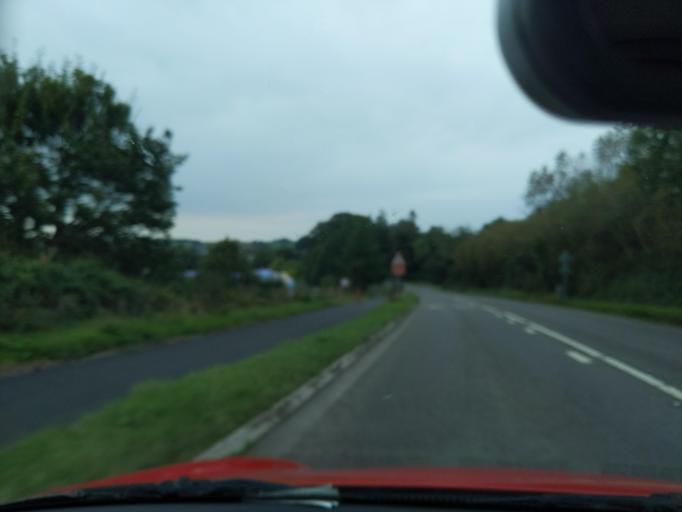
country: GB
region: England
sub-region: Devon
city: Okehampton
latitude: 50.8293
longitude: -4.0740
